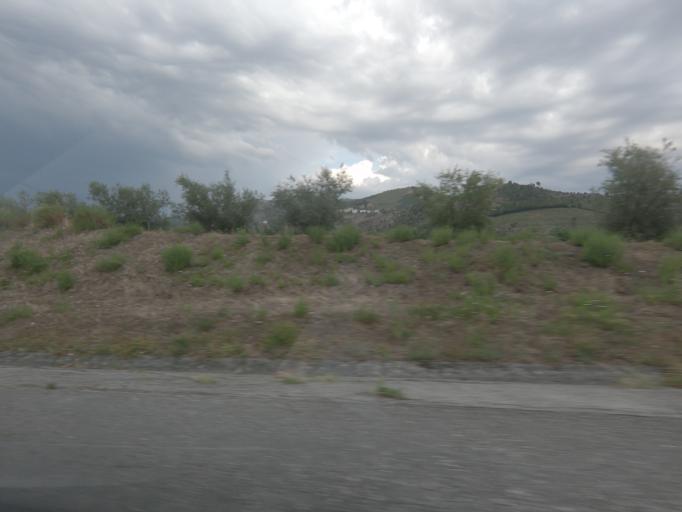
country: PT
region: Vila Real
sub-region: Peso da Regua
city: Peso da Regua
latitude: 41.1282
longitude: -7.7770
